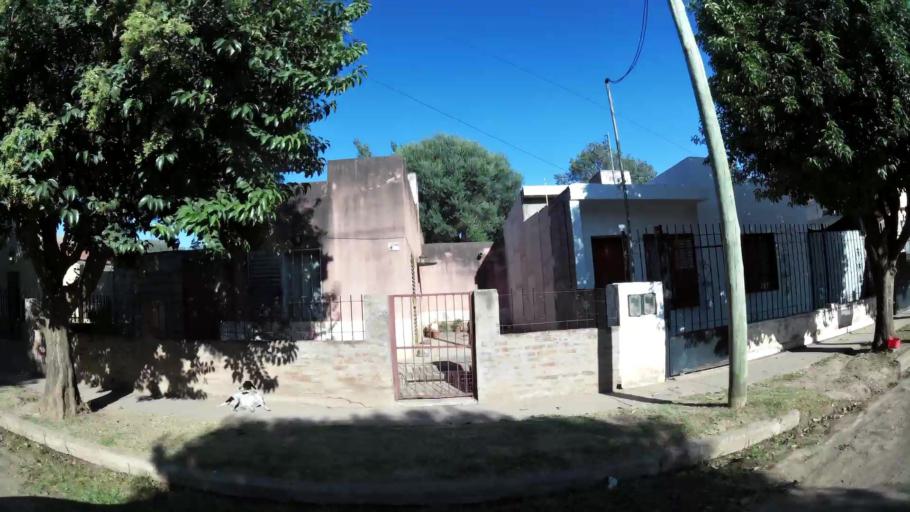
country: AR
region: Cordoba
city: Villa Allende
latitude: -31.3366
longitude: -64.2471
